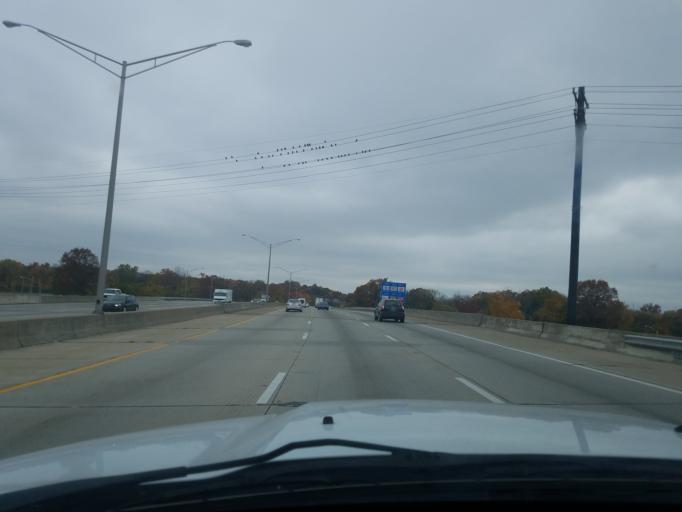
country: US
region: Kentucky
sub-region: Jefferson County
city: Shively
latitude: 38.1892
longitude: -85.7828
